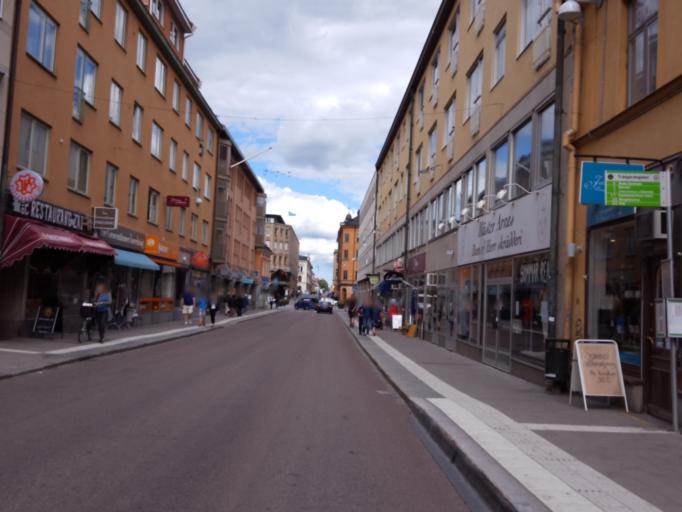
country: SE
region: Uppsala
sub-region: Uppsala Kommun
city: Uppsala
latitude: 59.8571
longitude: 17.6359
